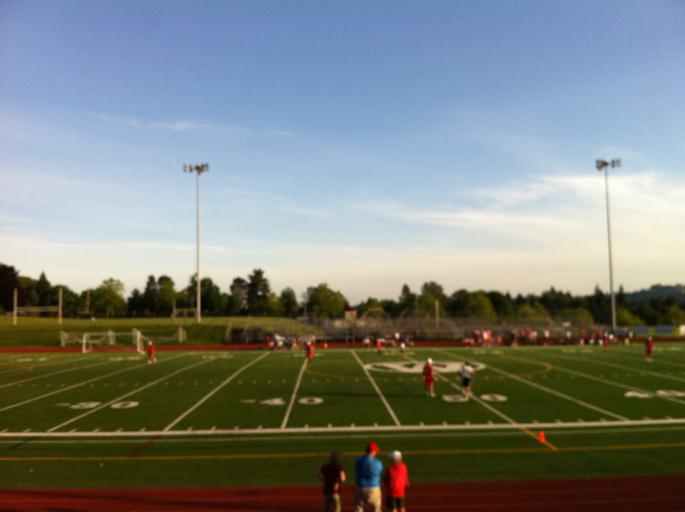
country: US
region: Oregon
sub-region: Multnomah County
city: Portland
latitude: 45.4782
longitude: -122.6920
